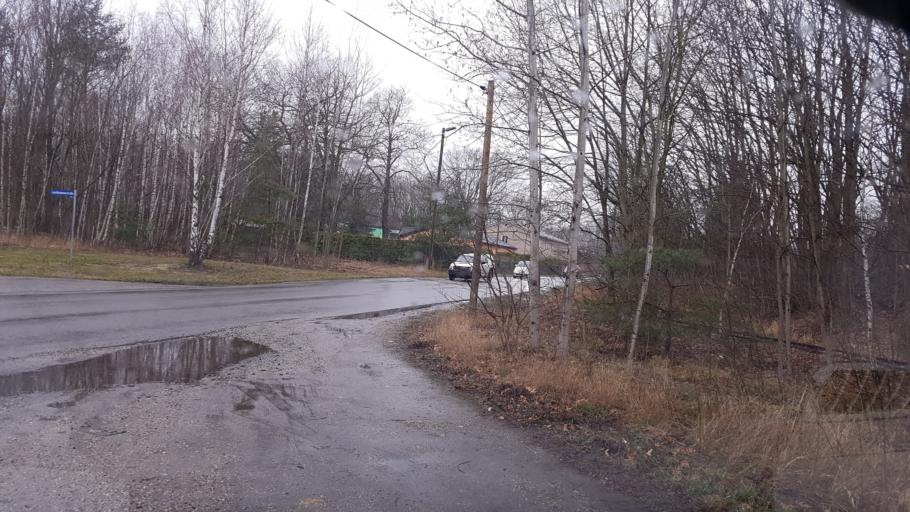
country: DE
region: Brandenburg
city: Schwarzheide
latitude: 51.4948
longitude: 13.8151
